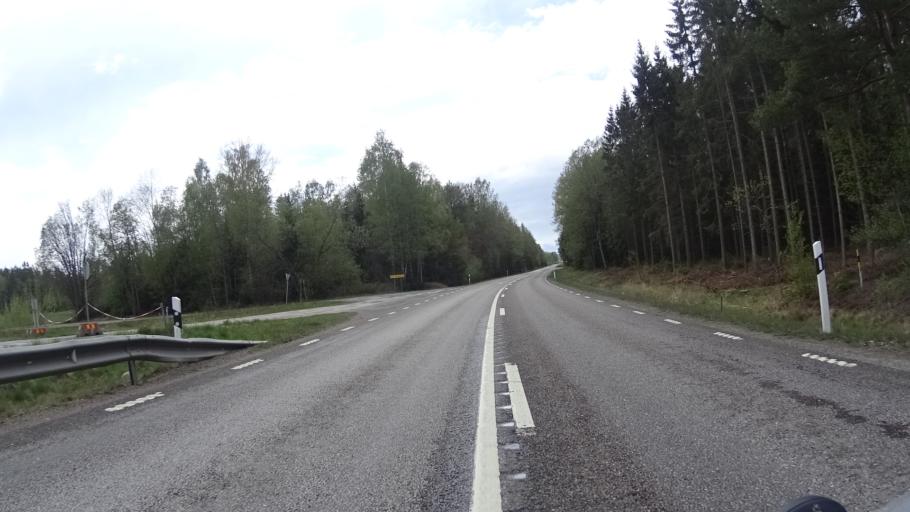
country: SE
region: Vaestra Goetaland
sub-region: Karlsborgs Kommun
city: Karlsborg
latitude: 58.4990
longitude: 14.4602
